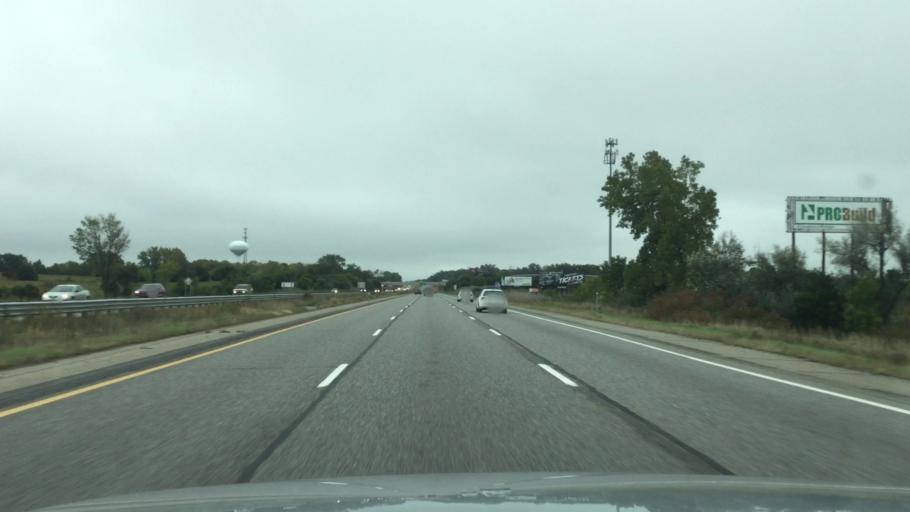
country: US
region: Michigan
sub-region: Genesee County
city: Grand Blanc
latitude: 42.8921
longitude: -83.6276
